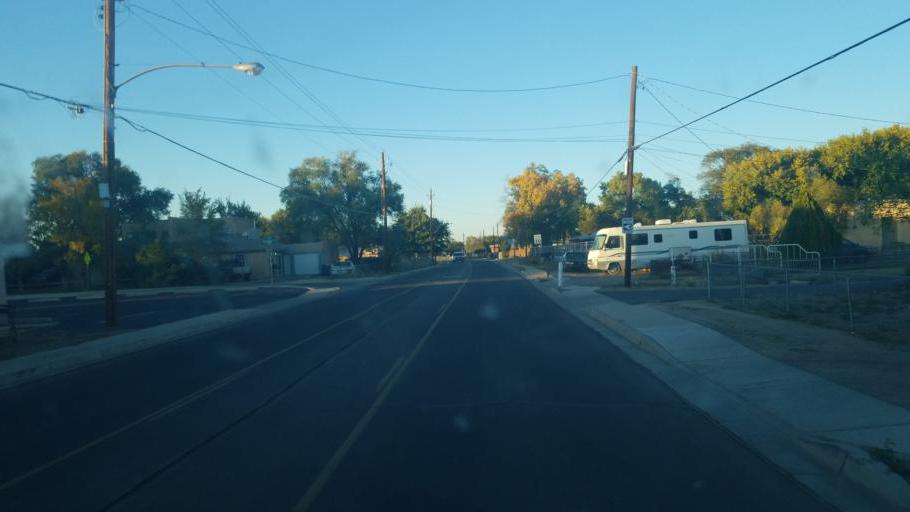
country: US
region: New Mexico
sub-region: Valencia County
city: Los Lunas
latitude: 34.8154
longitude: -106.7263
